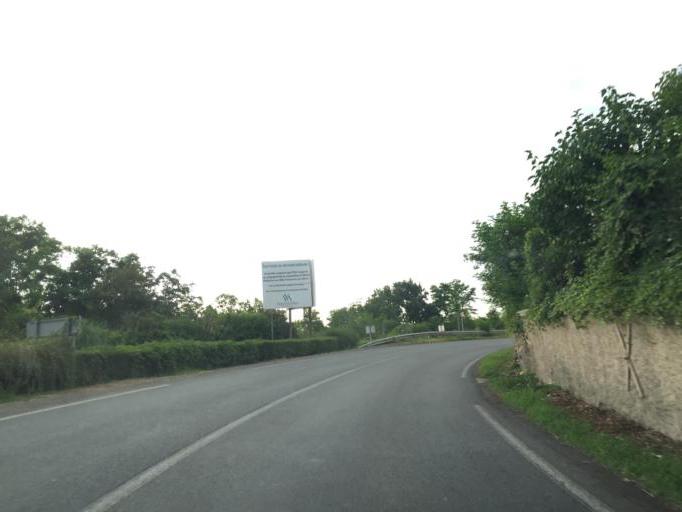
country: FR
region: Auvergne
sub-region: Departement de l'Allier
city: Saint-Germain-des-Fosses
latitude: 46.2389
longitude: 3.4276
